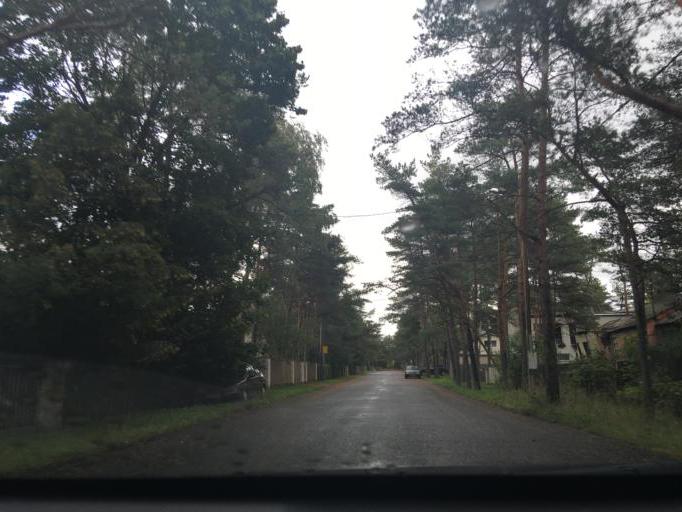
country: EE
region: Harju
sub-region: Saue vald
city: Laagri
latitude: 59.3702
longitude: 24.6706
